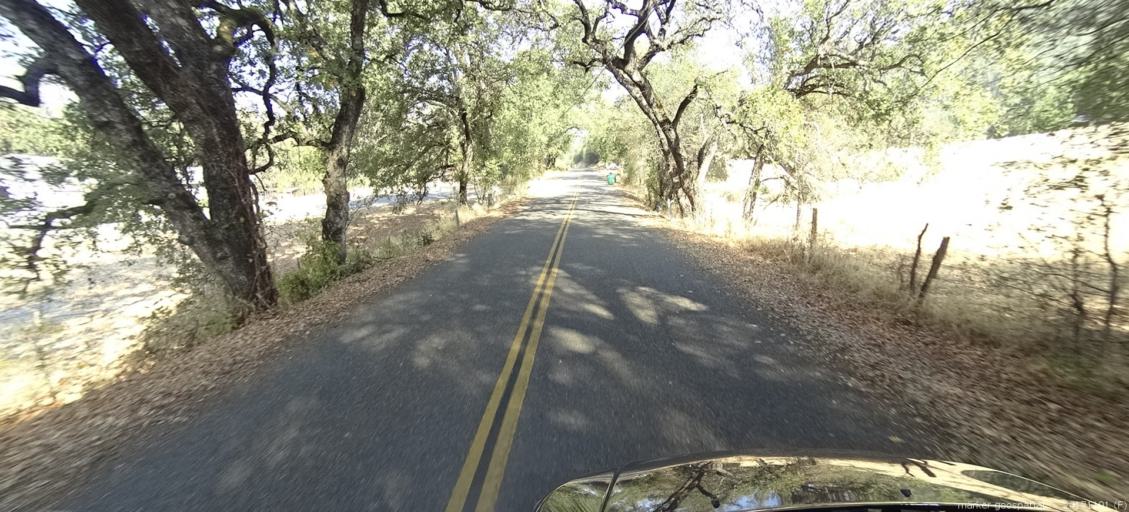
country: US
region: California
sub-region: Shasta County
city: Shasta Lake
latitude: 40.7127
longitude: -122.3285
